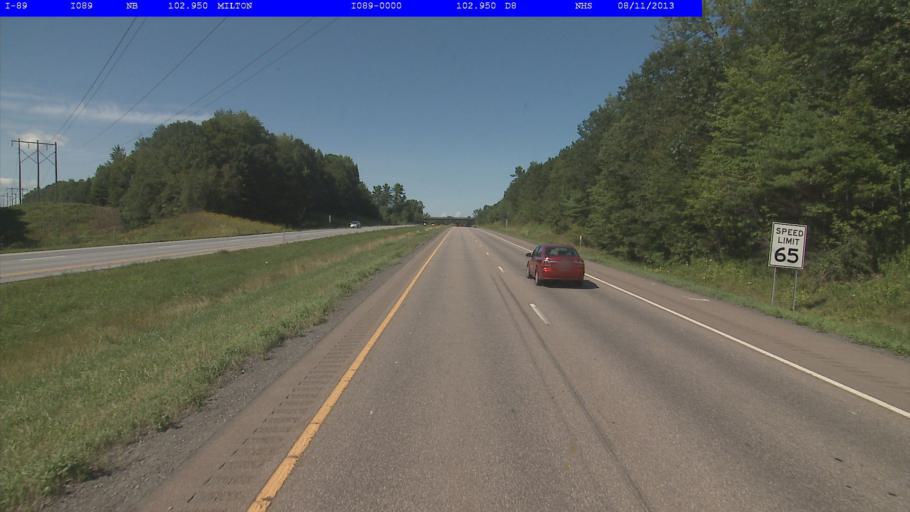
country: US
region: Vermont
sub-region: Chittenden County
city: Milton
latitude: 44.6559
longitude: -73.1389
